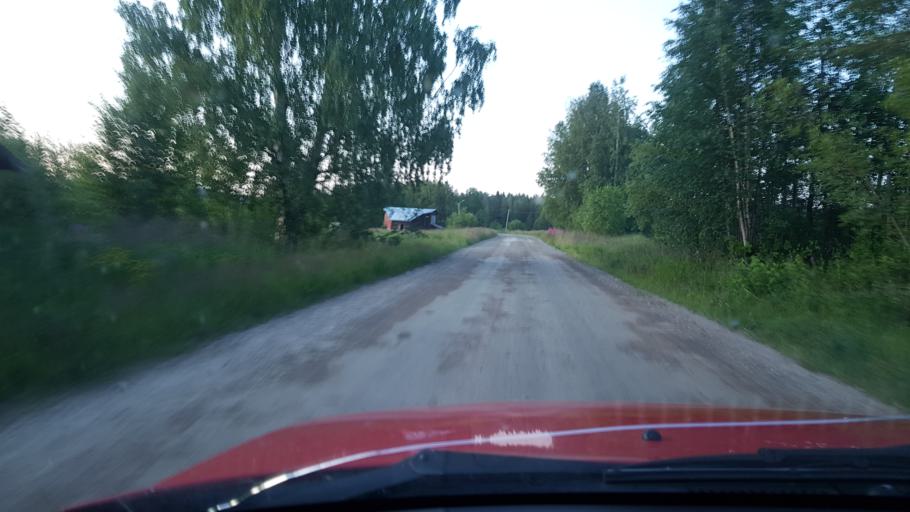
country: SE
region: Norrbotten
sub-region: Alvsbyns Kommun
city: AElvsbyn
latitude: 65.6990
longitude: 20.6749
